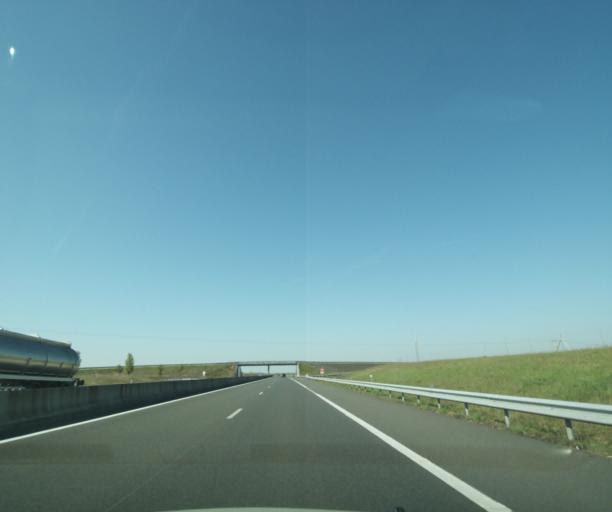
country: FR
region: Centre
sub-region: Departement du Loiret
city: Ascheres-le-Marche
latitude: 48.0772
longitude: 1.9778
